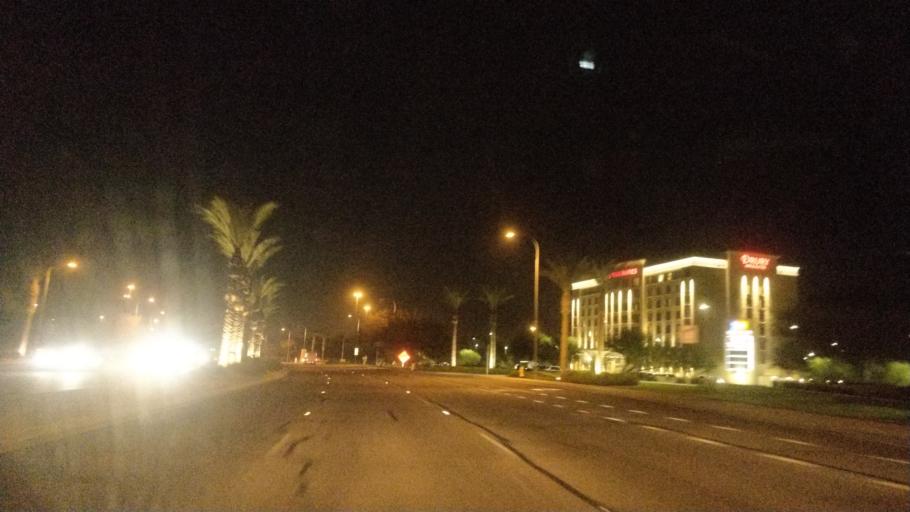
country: US
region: Arizona
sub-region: Maricopa County
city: Chandler
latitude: 33.2877
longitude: -111.8911
